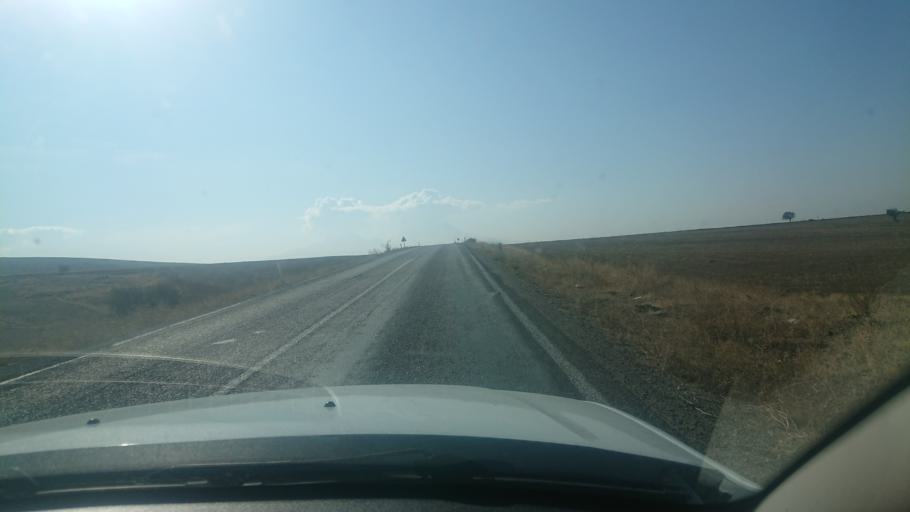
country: TR
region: Aksaray
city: Guzelyurt
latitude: 38.3094
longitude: 34.3267
